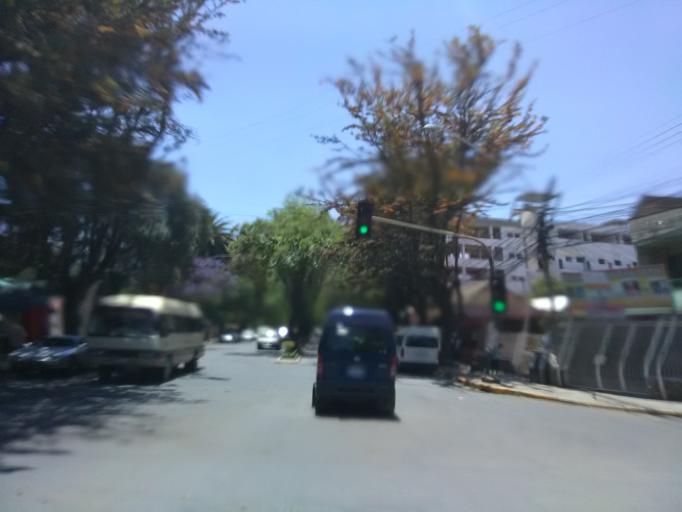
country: BO
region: Cochabamba
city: Cochabamba
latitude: -17.3887
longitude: -66.1494
